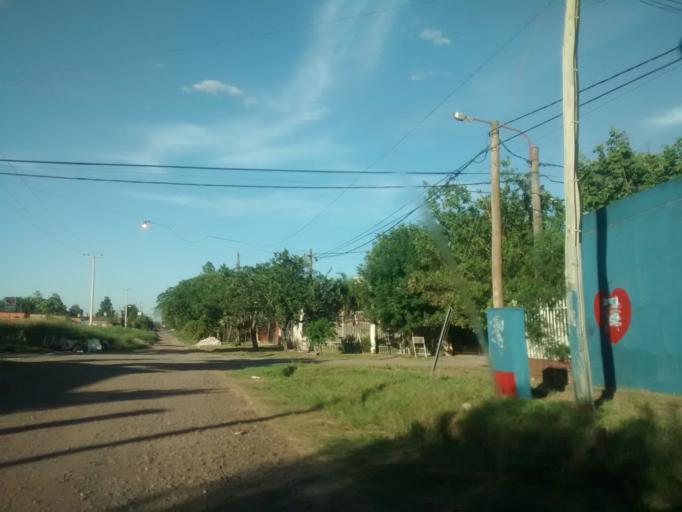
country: AR
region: Chaco
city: Fontana
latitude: -27.4531
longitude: -59.0223
